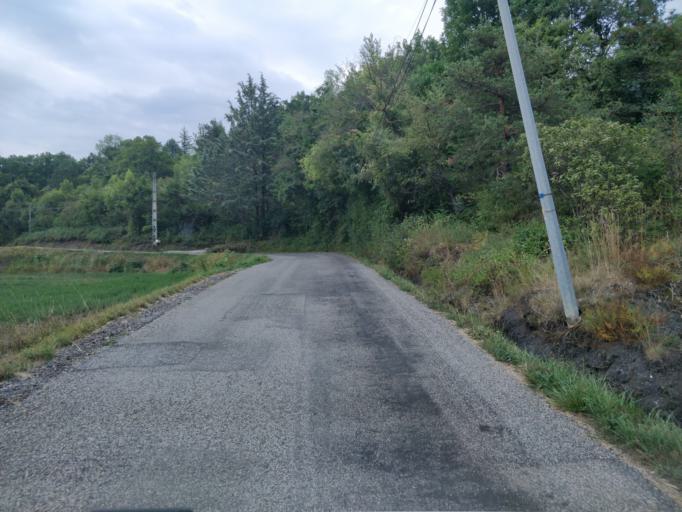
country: FR
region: Provence-Alpes-Cote d'Azur
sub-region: Departement des Alpes-de-Haute-Provence
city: Le Brusquet
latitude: 44.1308
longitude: 6.2757
